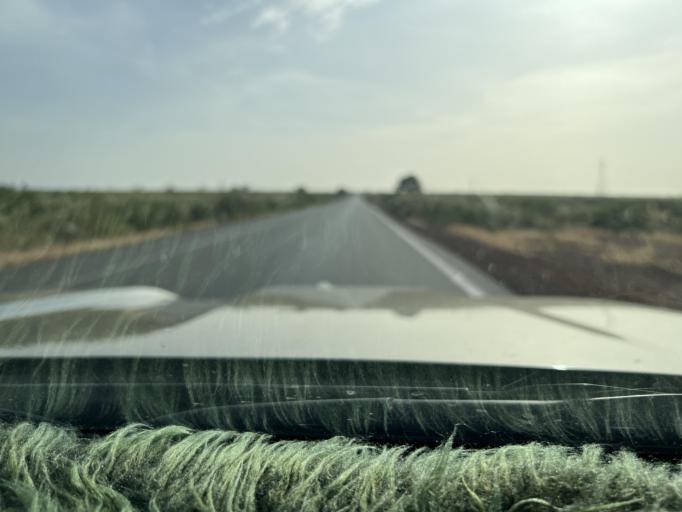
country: ML
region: Segou
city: Baroueli
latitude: 12.9581
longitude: -6.7256
